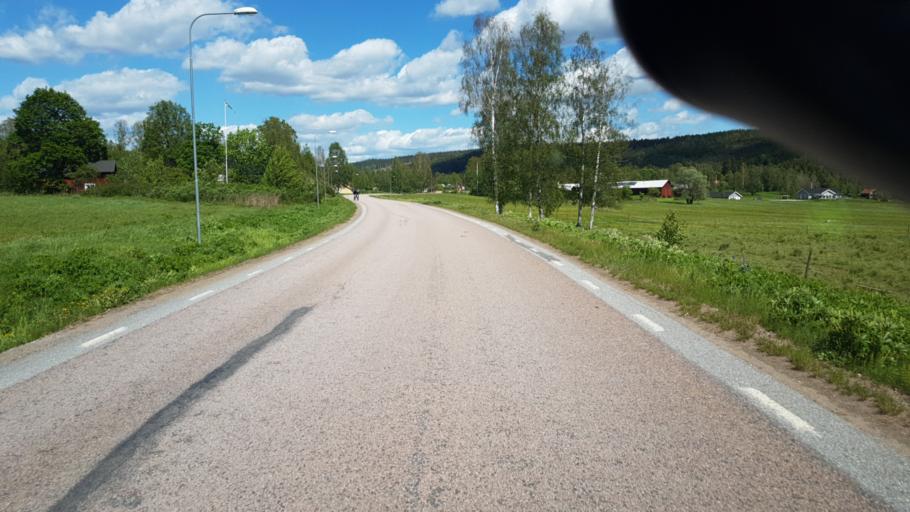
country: SE
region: Vaermland
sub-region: Arvika Kommun
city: Arvika
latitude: 59.7474
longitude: 12.8170
